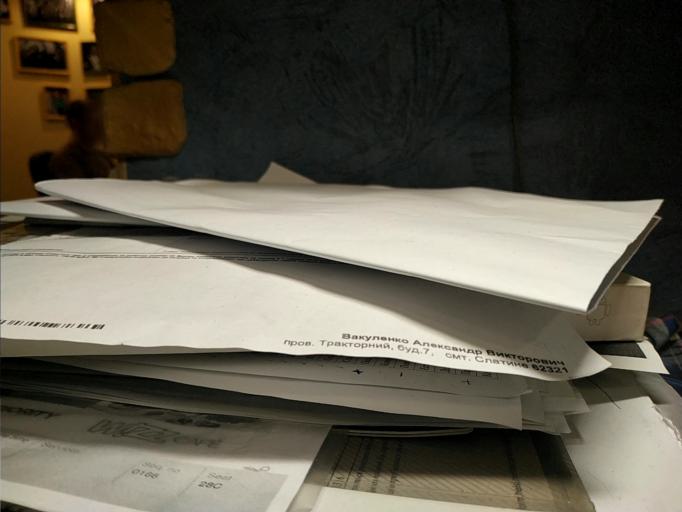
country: RU
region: Tverskaya
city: Zubtsov
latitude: 56.1359
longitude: 34.4829
